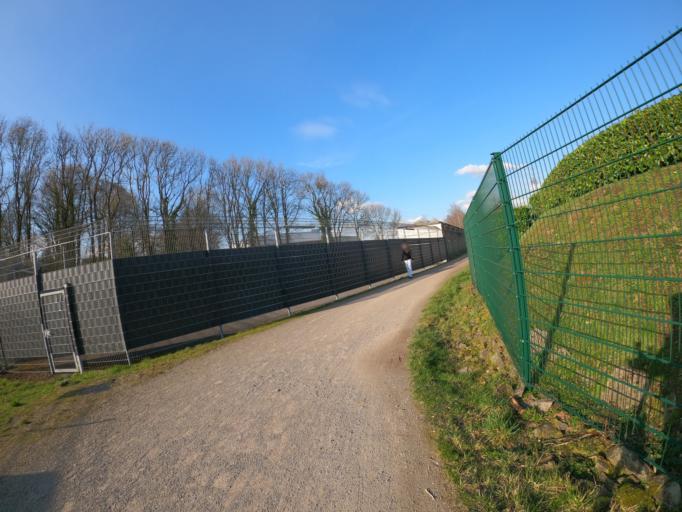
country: DE
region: North Rhine-Westphalia
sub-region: Regierungsbezirk Dusseldorf
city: Remscheid
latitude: 51.2074
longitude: 7.1377
